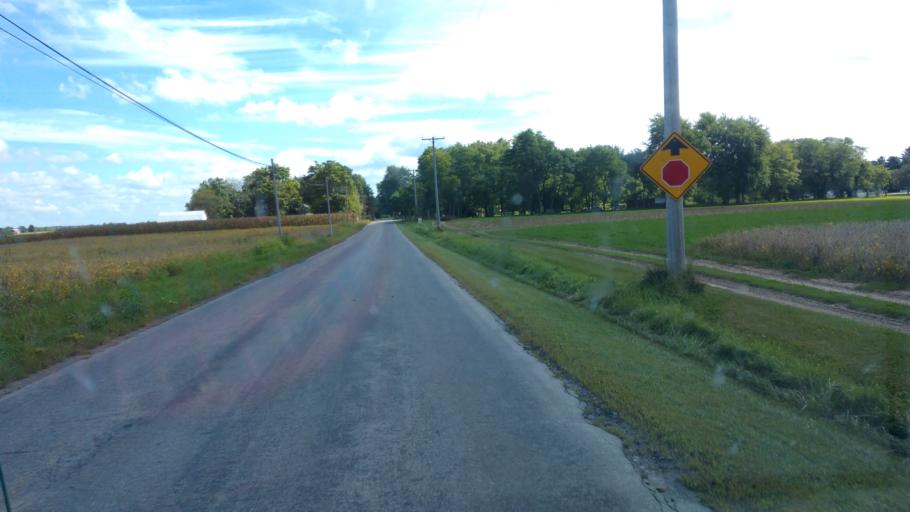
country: US
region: Ohio
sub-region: Richland County
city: Shelby
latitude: 40.9100
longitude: -82.6322
